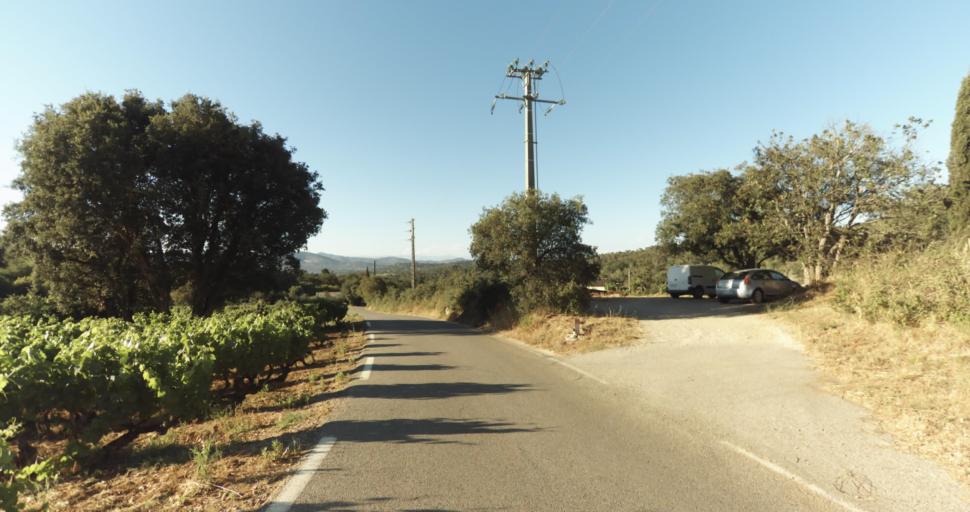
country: FR
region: Provence-Alpes-Cote d'Azur
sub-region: Departement du Var
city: Gassin
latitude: 43.2266
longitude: 6.5927
